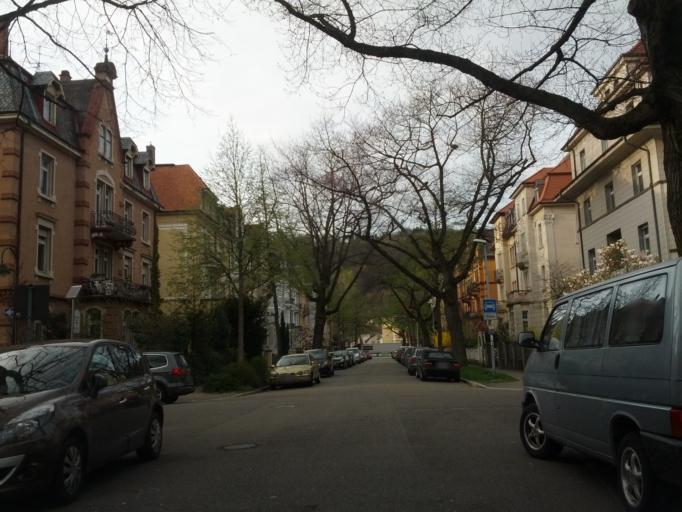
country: DE
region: Baden-Wuerttemberg
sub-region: Freiburg Region
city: Freiburg
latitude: 47.9865
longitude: 7.8624
